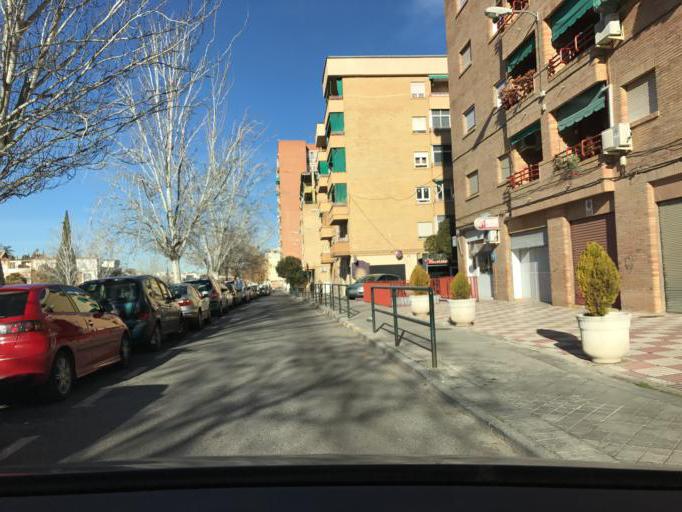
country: ES
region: Andalusia
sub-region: Provincia de Granada
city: Huetor Vega
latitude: 37.1642
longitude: -3.5799
